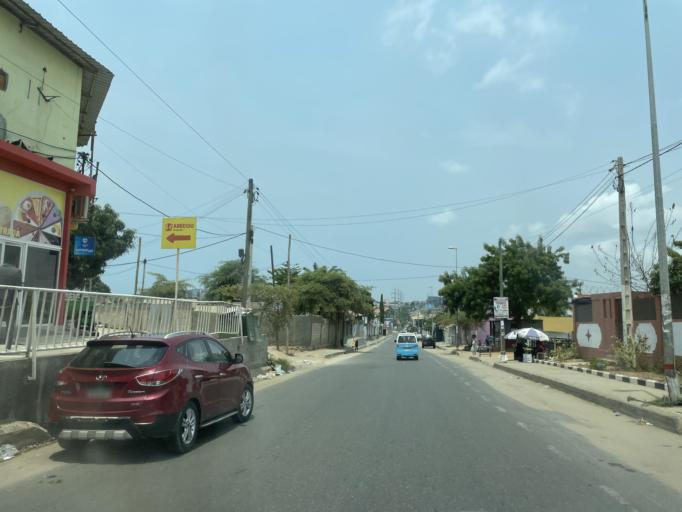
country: AO
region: Luanda
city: Luanda
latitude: -8.9366
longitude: 13.1704
